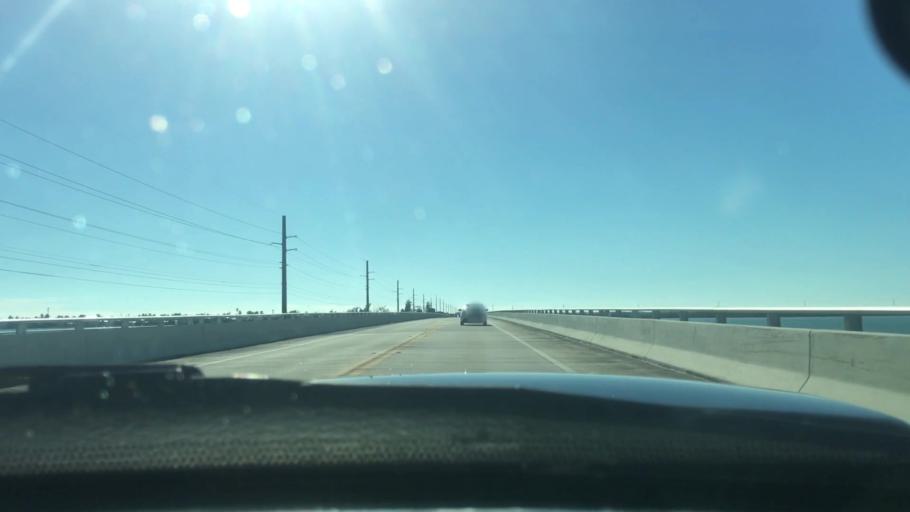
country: US
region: Florida
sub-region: Monroe County
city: Big Coppitt Key
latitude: 24.6337
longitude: -81.5857
